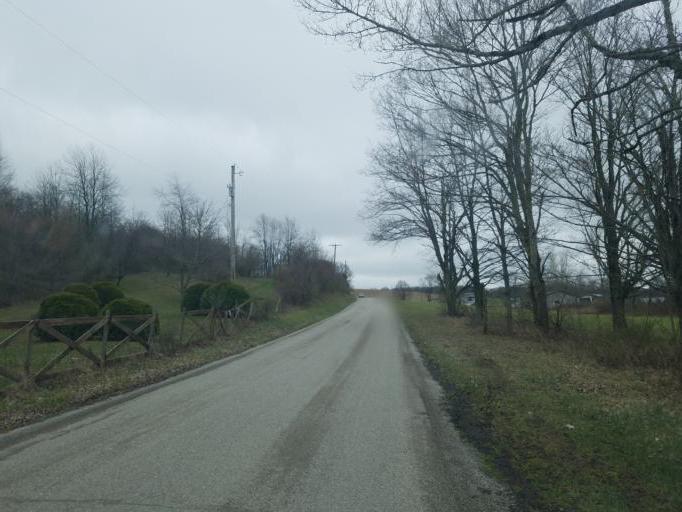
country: US
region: Ohio
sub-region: Sandusky County
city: Bellville
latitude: 40.5586
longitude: -82.4732
